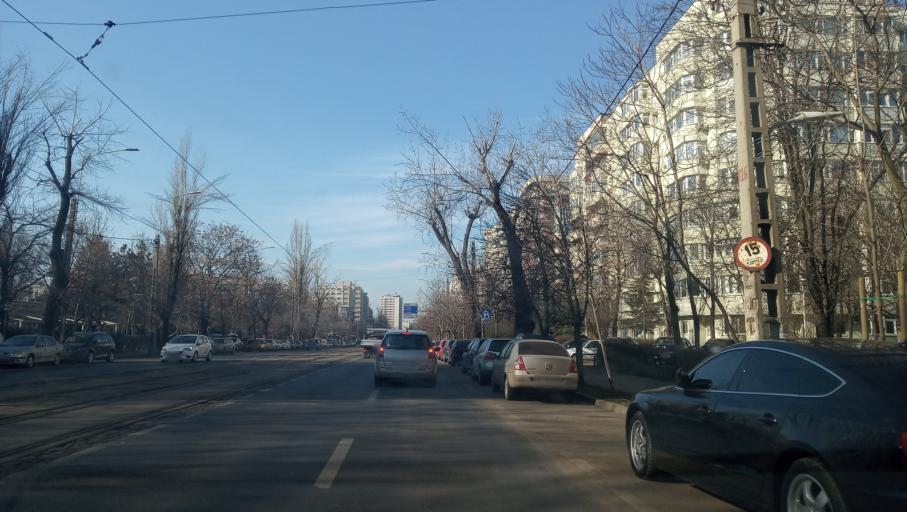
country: RO
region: Ilfov
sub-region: Comuna Fundeni-Dobroesti
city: Fundeni
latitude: 44.4359
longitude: 26.1632
